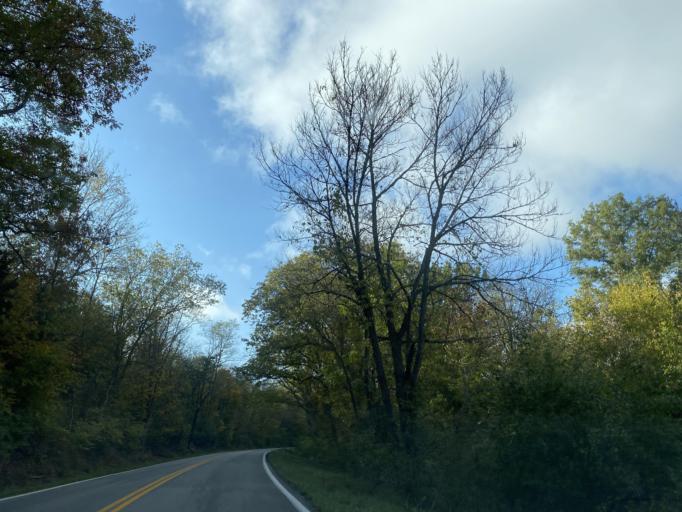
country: US
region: Kentucky
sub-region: Pendleton County
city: Falmouth
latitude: 38.7096
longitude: -84.3020
